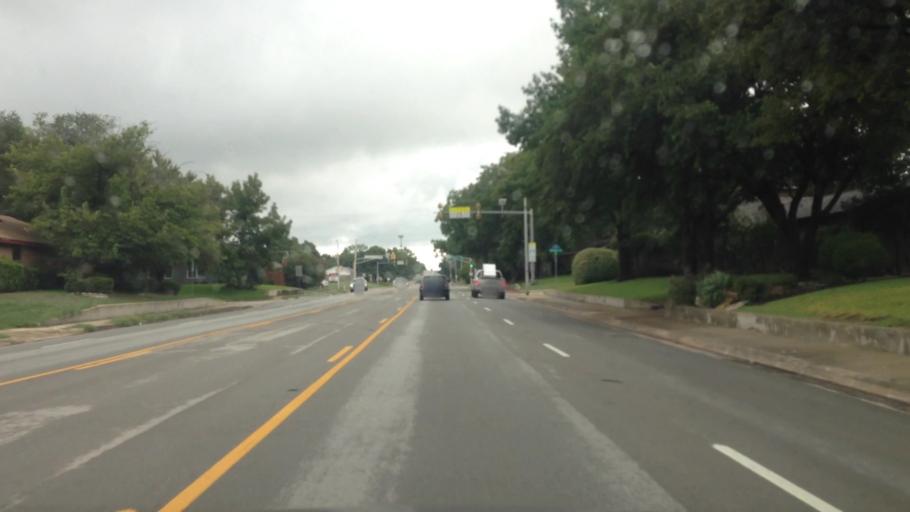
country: US
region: Texas
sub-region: Tarrant County
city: Edgecliff Village
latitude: 32.6565
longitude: -97.3959
